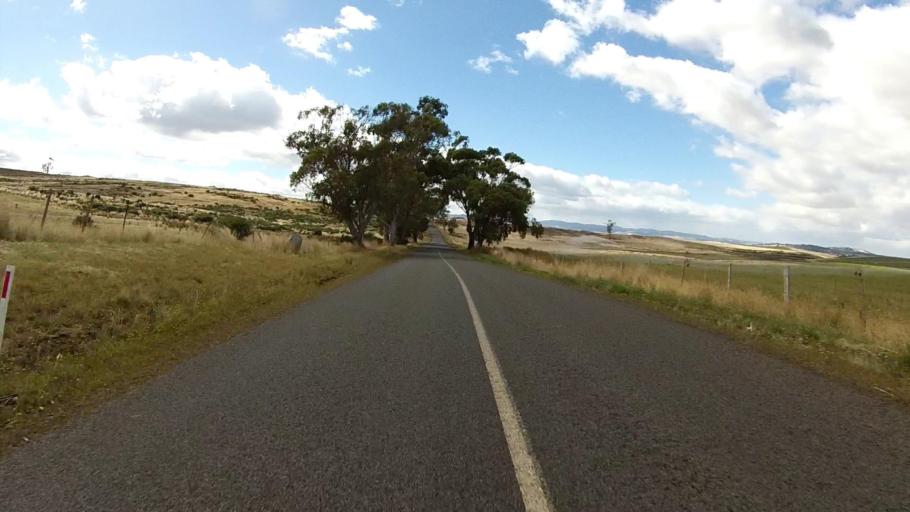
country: AU
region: Tasmania
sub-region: Northern Midlands
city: Evandale
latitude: -41.7038
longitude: 147.3860
